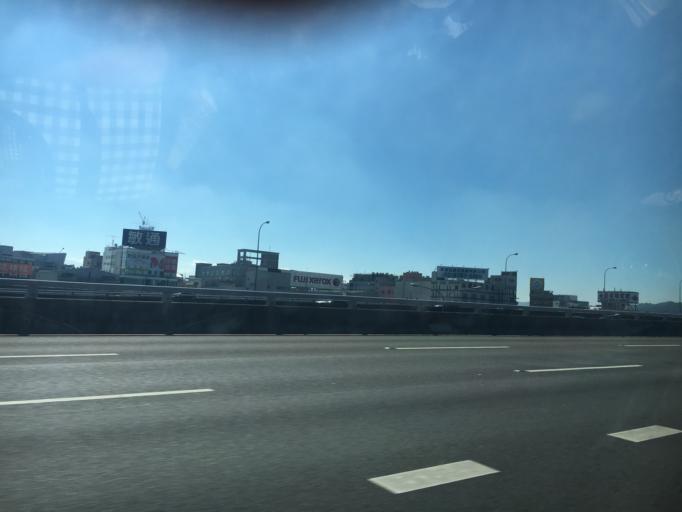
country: TW
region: Taipei
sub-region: Taipei
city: Banqiao
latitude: 25.0731
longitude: 121.4521
